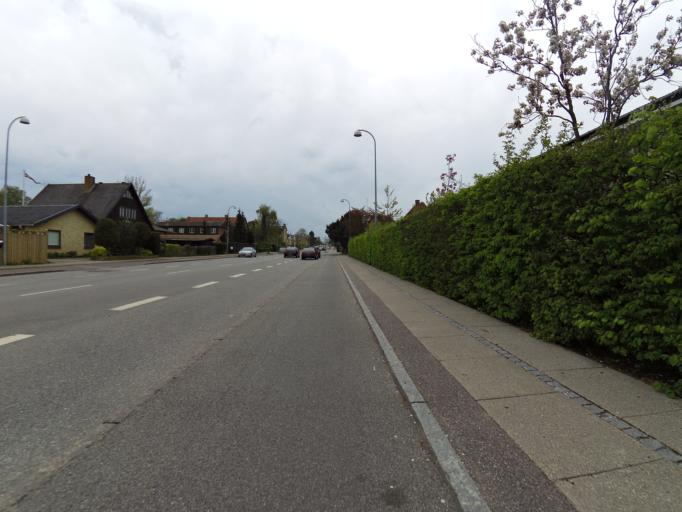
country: DK
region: Capital Region
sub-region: Gladsaxe Municipality
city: Buddinge
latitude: 55.7420
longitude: 12.5094
